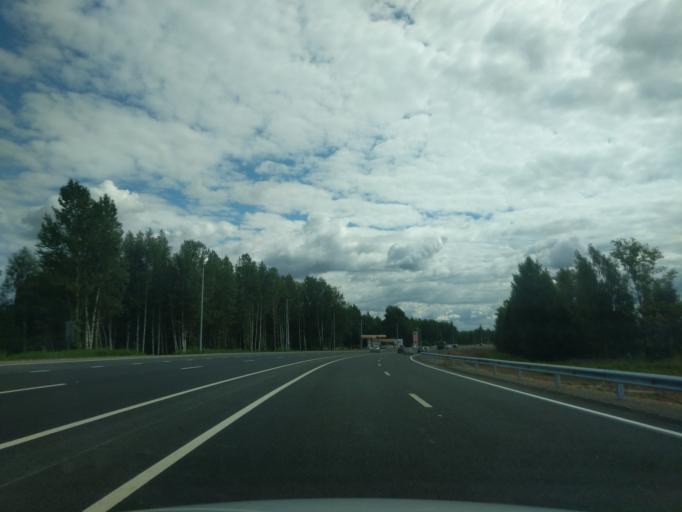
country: RU
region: Kostroma
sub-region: Kostromskoy Rayon
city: Kostroma
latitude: 57.7393
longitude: 40.8637
